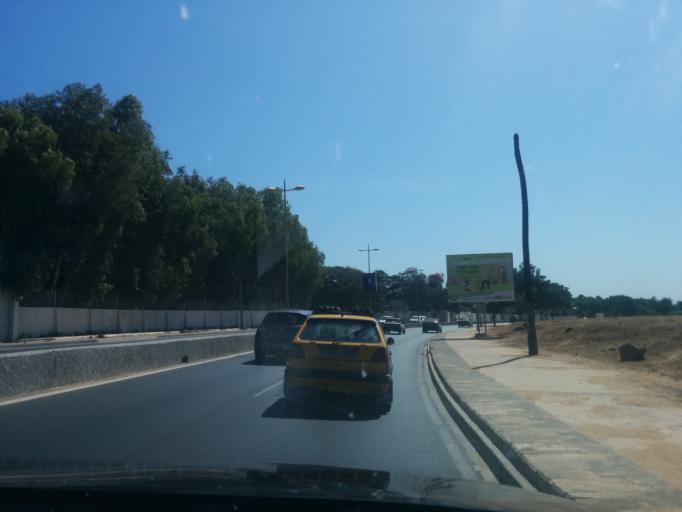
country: SN
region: Dakar
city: Mermoz Boabab
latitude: 14.6994
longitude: -17.4724
